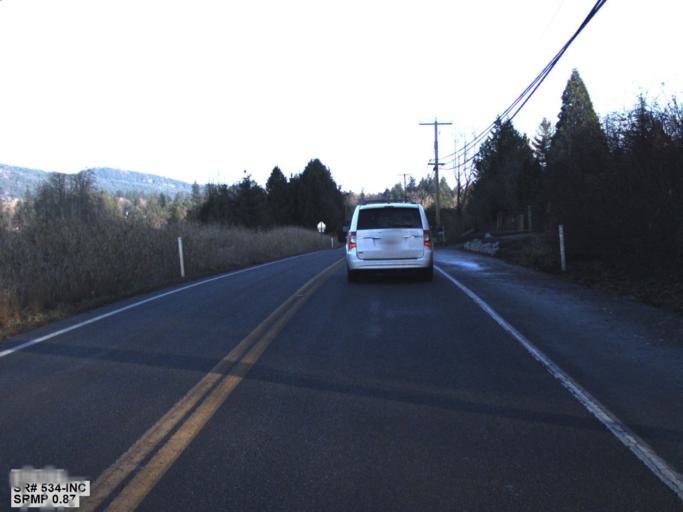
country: US
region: Washington
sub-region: Skagit County
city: Mount Vernon
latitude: 48.3408
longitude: -122.3160
